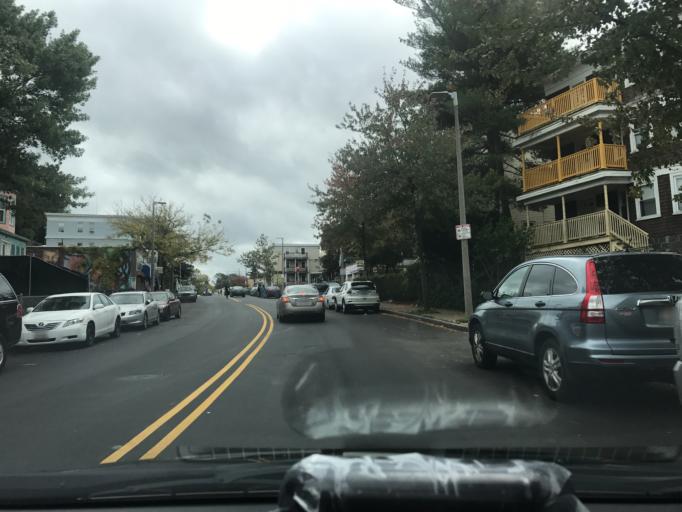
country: US
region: Massachusetts
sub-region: Norfolk County
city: Milton
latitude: 42.2844
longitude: -71.0716
